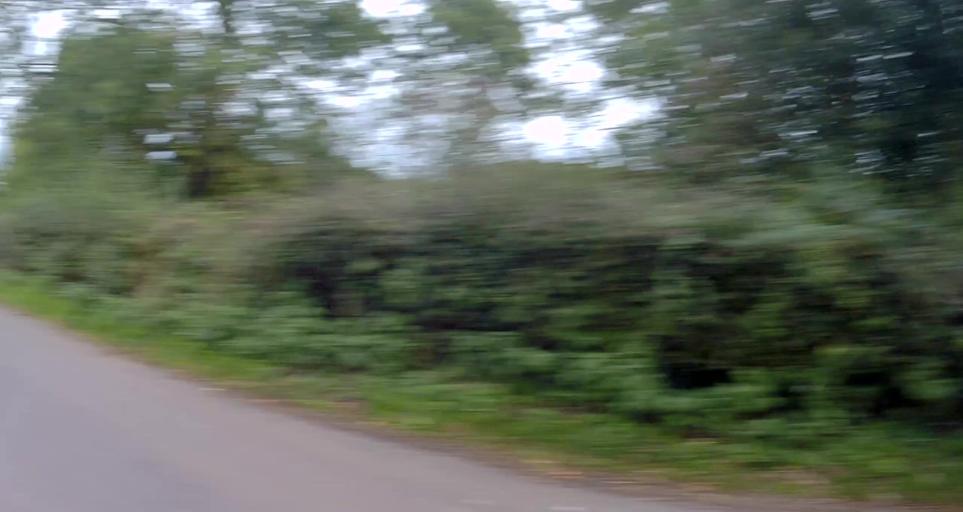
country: GB
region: England
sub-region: Hampshire
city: Four Marks
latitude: 51.1376
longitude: -1.0813
